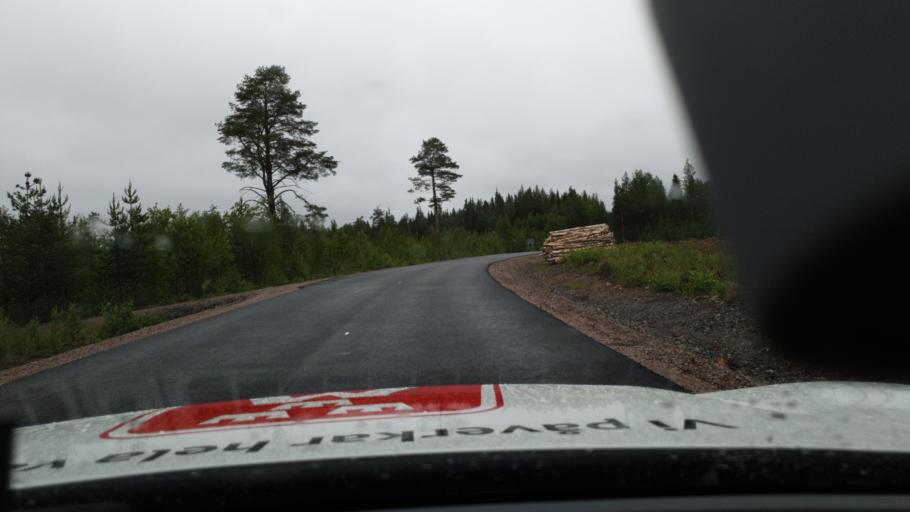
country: SE
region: Norrbotten
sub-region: Overtornea Kommun
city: OEvertornea
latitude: 66.5469
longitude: 23.3469
